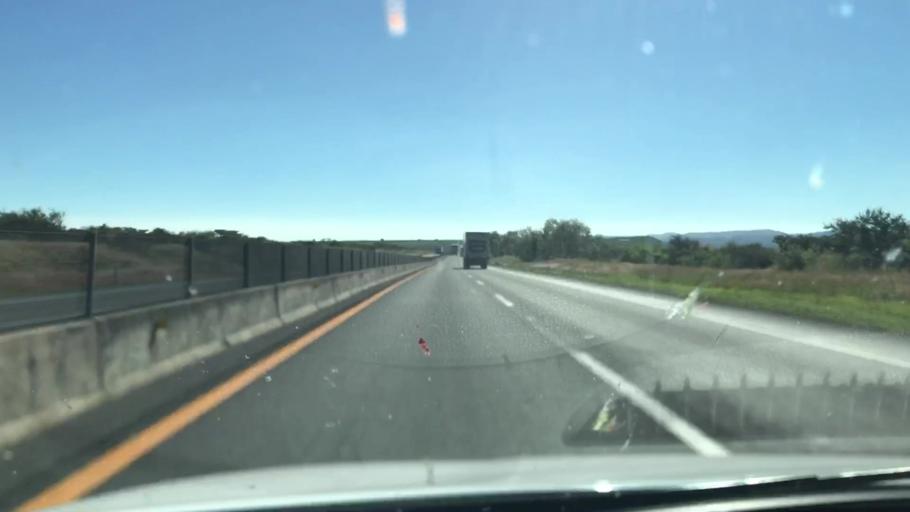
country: MX
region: Jalisco
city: Valle de Guadalupe
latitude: 21.0503
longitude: -102.5305
